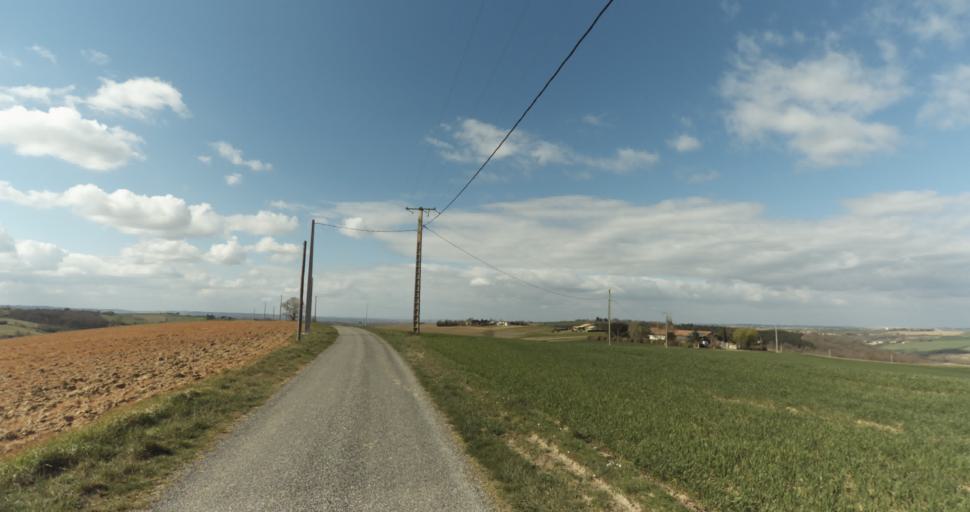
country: FR
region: Midi-Pyrenees
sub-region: Departement de la Haute-Garonne
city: Auterive
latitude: 43.3637
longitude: 1.5100
